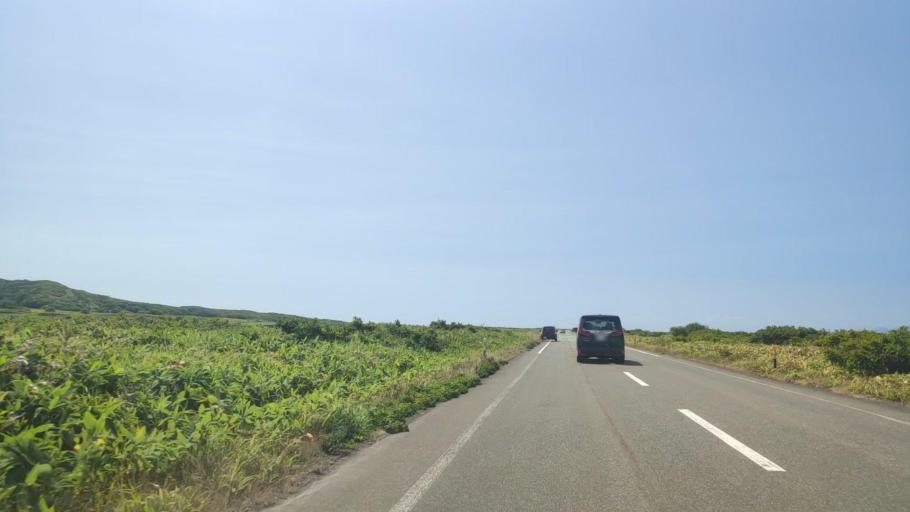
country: JP
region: Hokkaido
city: Wakkanai
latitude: 45.2413
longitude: 141.5814
